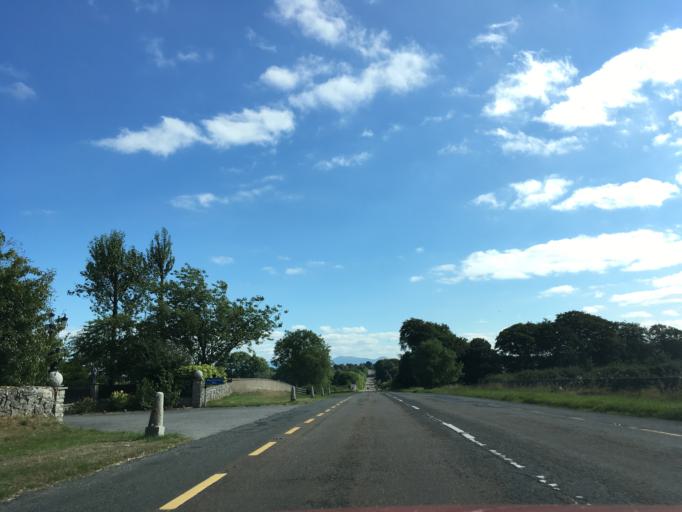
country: IE
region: Munster
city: Cashel
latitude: 52.4911
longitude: -7.8902
